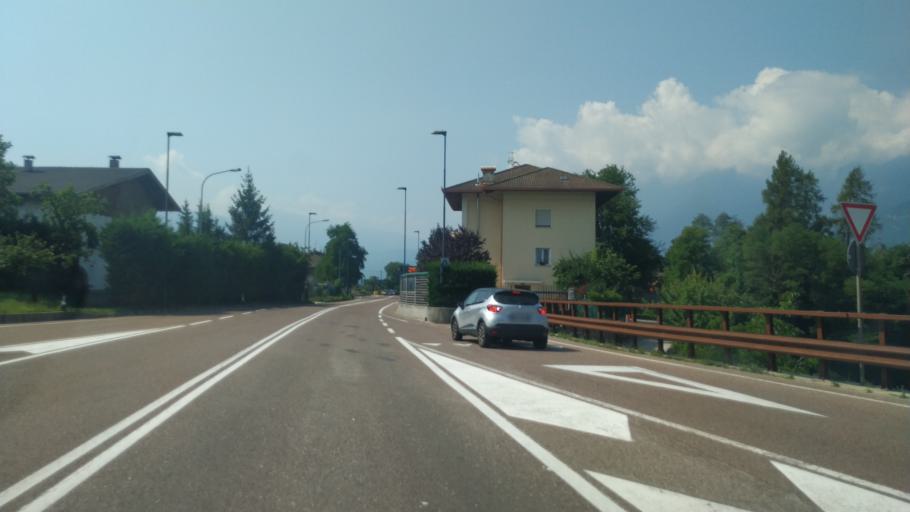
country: IT
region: Trentino-Alto Adige
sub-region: Provincia di Trento
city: Taio
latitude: 46.2961
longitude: 11.0681
